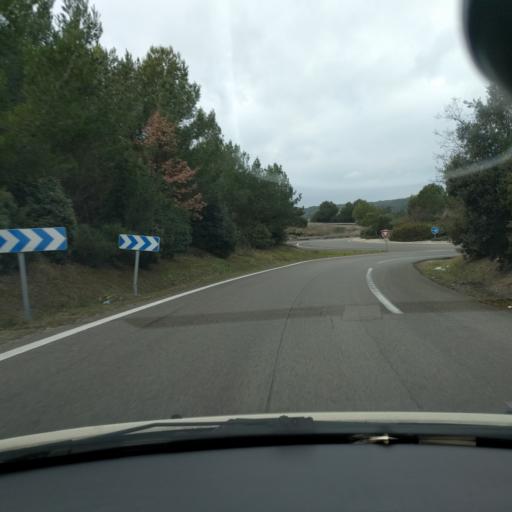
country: FR
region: Provence-Alpes-Cote d'Azur
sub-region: Departement des Bouches-du-Rhone
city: Bouc-Bel-Air
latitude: 43.4285
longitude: 5.4048
